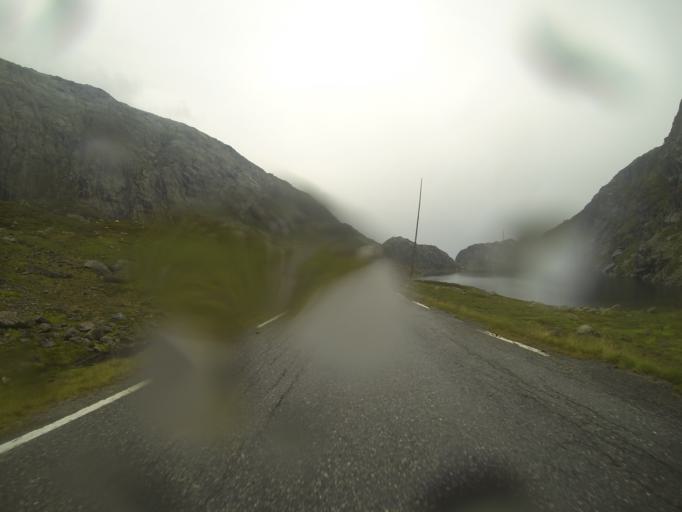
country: NO
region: Hordaland
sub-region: Odda
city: Odda
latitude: 59.7715
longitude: 6.7429
